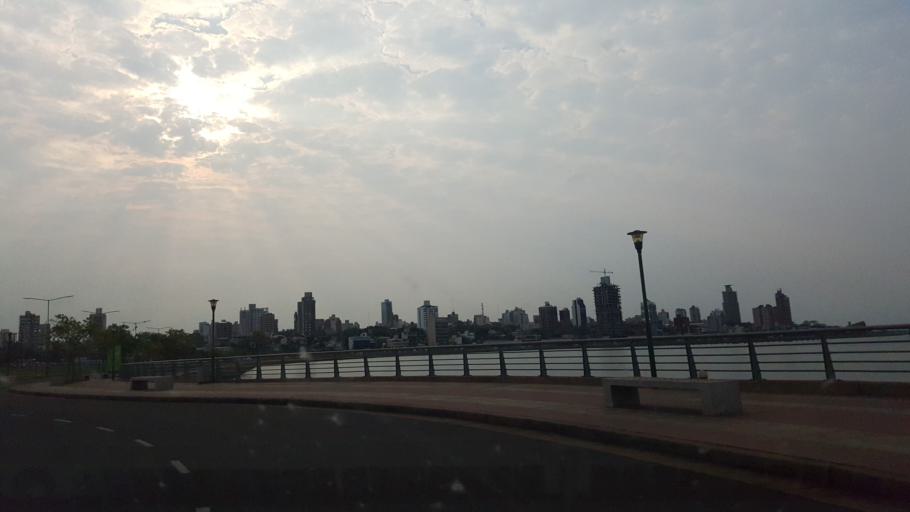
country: AR
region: Misiones
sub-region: Departamento de Capital
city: Posadas
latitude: -27.3747
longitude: -55.8805
